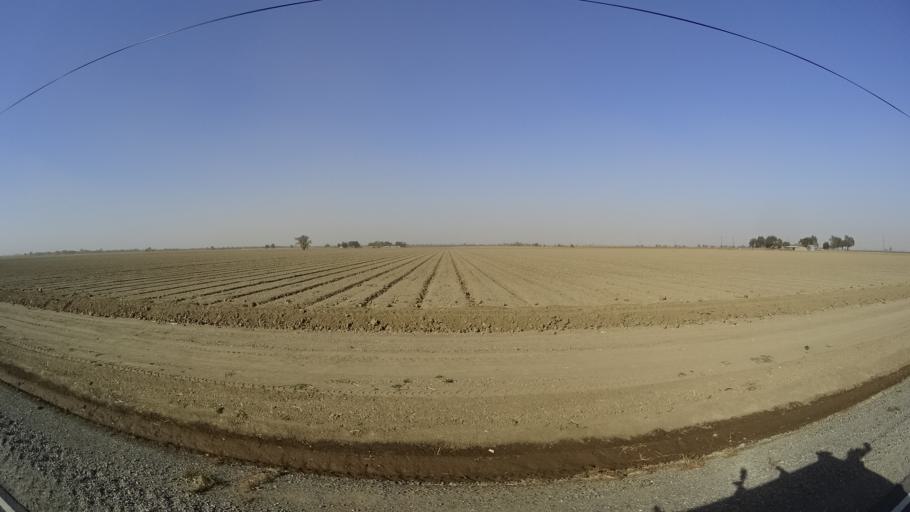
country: US
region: California
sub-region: Yolo County
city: Woodland
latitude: 38.7934
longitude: -121.7913
